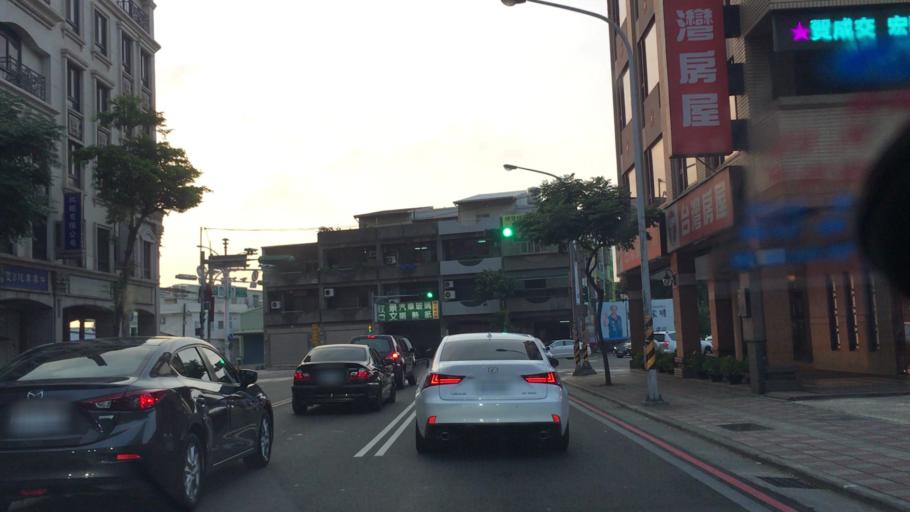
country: TW
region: Taiwan
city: Taoyuan City
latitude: 24.9933
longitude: 121.2783
